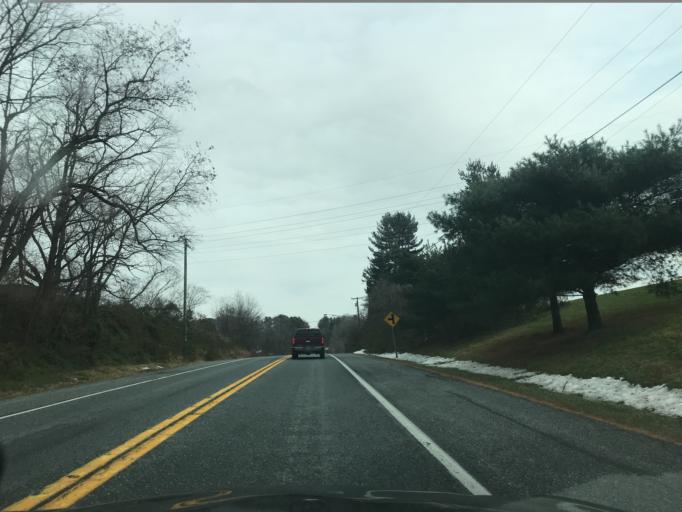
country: US
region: Maryland
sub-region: Harford County
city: Jarrettsville
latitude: 39.6656
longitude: -76.4332
